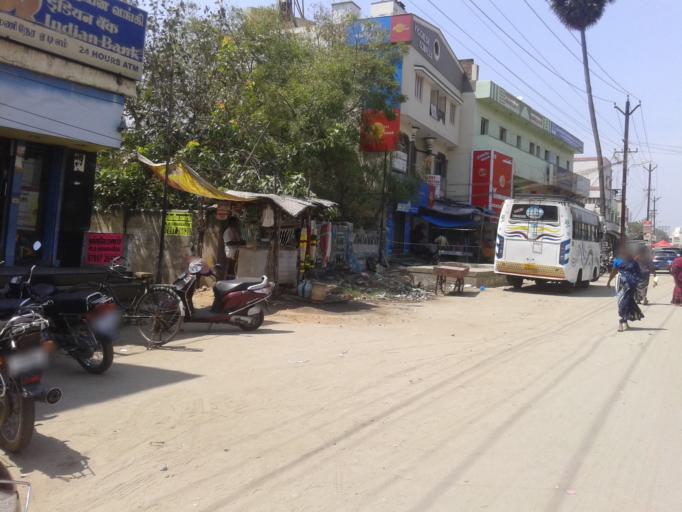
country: IN
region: Tamil Nadu
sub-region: Madurai
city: Madurai
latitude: 9.9314
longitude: 78.0942
